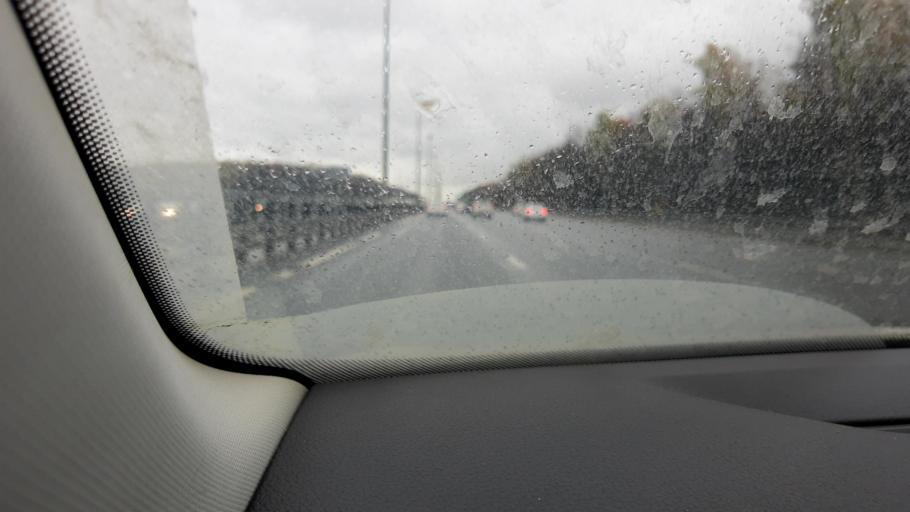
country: RU
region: Moskovskaya
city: Annino
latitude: 55.5886
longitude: 37.2767
